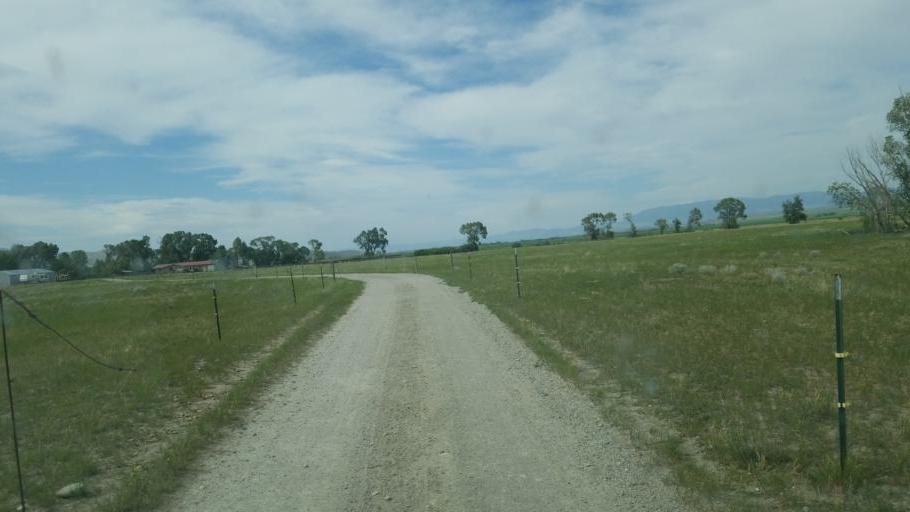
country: US
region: Montana
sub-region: Broadwater County
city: Townsend
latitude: 46.1857
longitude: -111.4809
